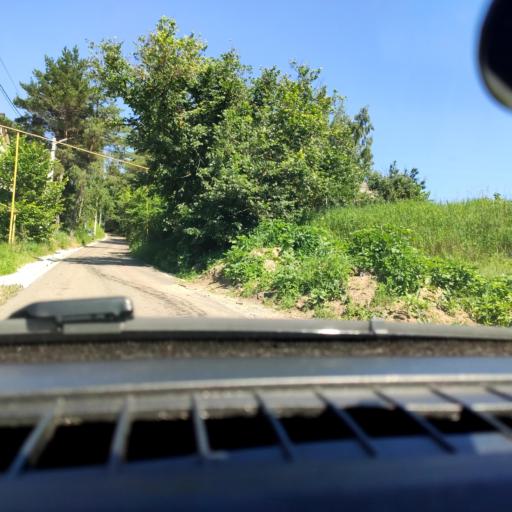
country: RU
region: Voronezj
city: Podgornoye
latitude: 51.7884
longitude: 39.1343
